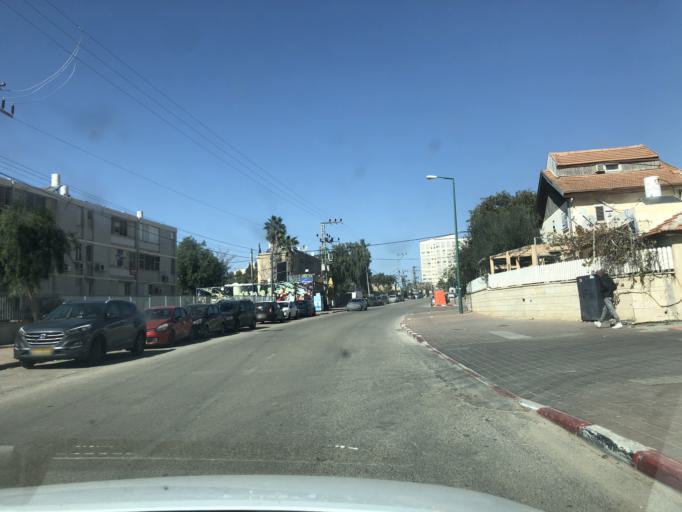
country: IL
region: Southern District
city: Beersheba
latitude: 31.2595
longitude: 34.7950
